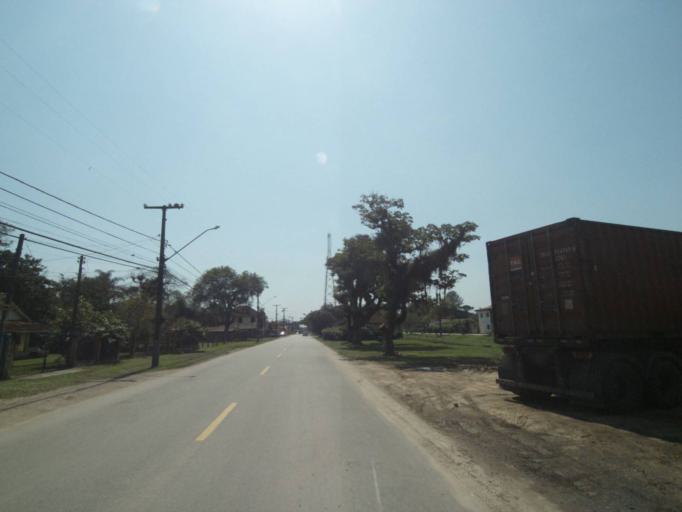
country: BR
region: Parana
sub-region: Paranagua
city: Paranagua
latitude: -25.5567
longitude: -48.6272
